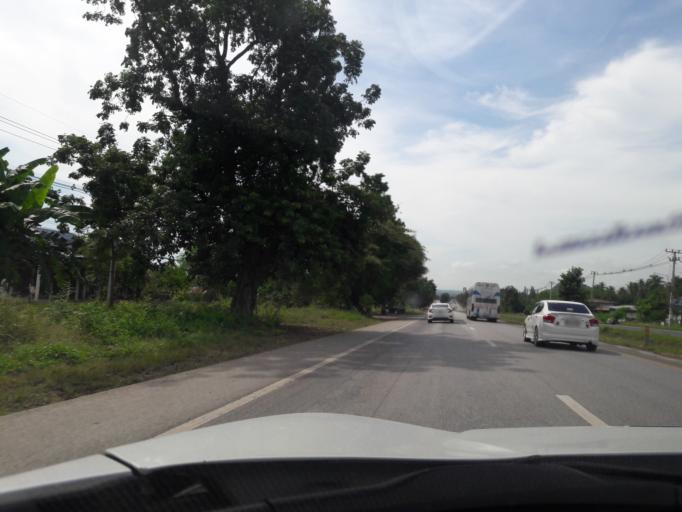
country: TH
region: Lop Buri
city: Chai Badan
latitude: 15.2430
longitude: 101.1262
